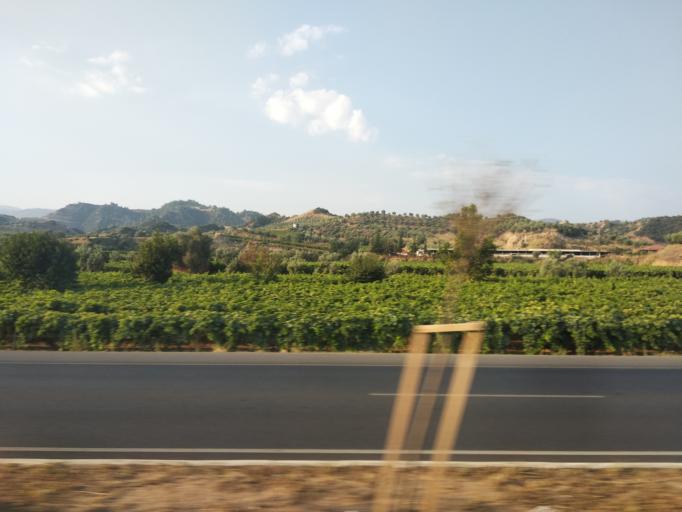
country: TR
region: Manisa
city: Ahmetli
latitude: 38.5080
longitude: 27.9876
